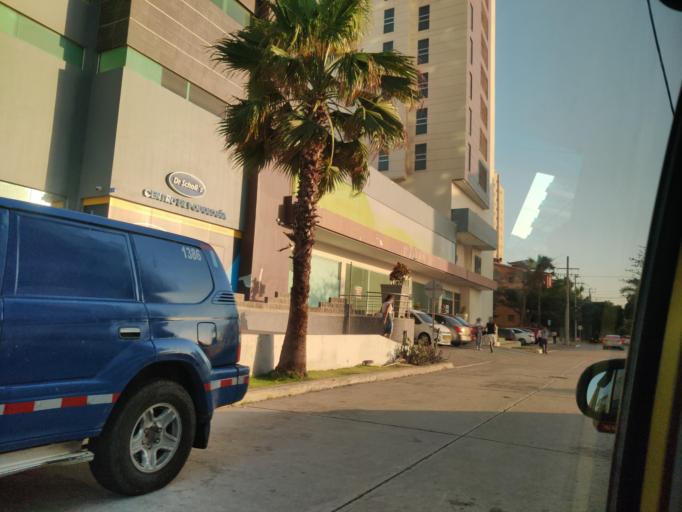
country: CO
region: Atlantico
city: Barranquilla
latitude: 11.0142
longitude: -74.8368
